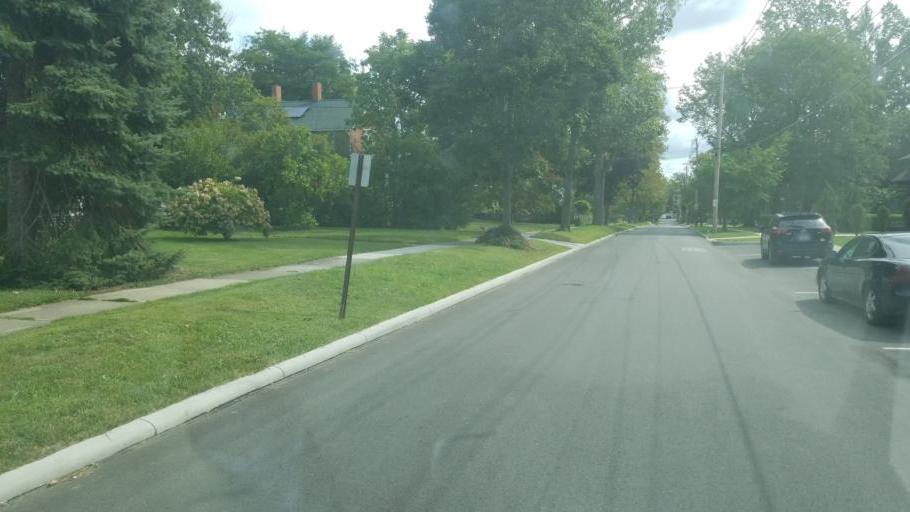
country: US
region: Ohio
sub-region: Lorain County
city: Oberlin
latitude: 41.2870
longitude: -82.2248
